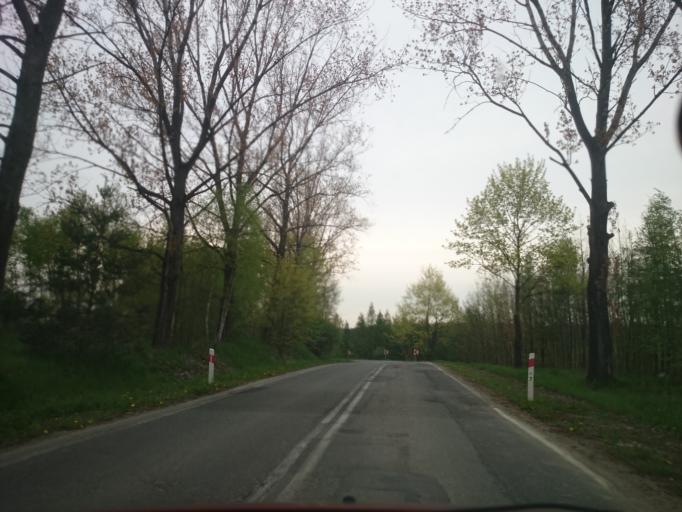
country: PL
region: Lower Silesian Voivodeship
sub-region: Powiat strzelinski
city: Przeworno
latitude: 50.6438
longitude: 17.1795
